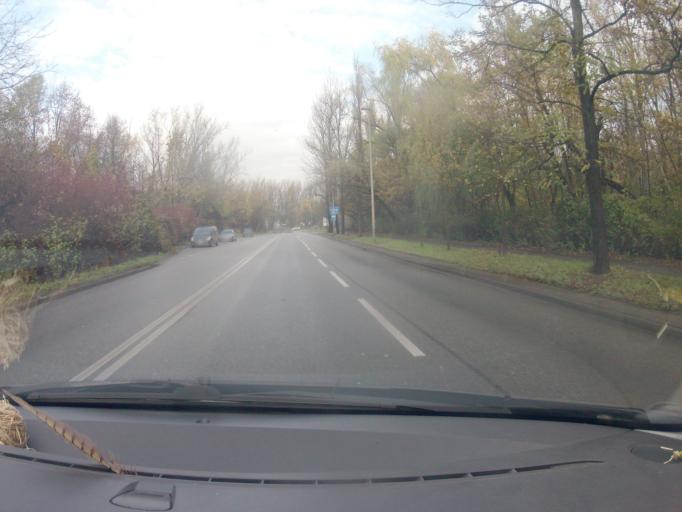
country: PL
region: Lesser Poland Voivodeship
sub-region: Powiat wielicki
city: Kokotow
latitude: 50.0773
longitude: 20.0627
